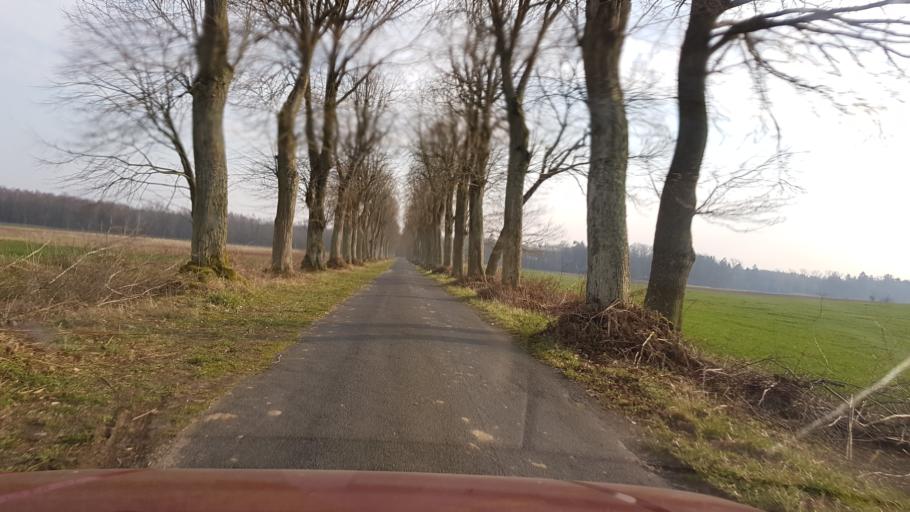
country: PL
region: West Pomeranian Voivodeship
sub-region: Powiat bialogardzki
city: Bialogard
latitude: 54.0844
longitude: 15.9750
